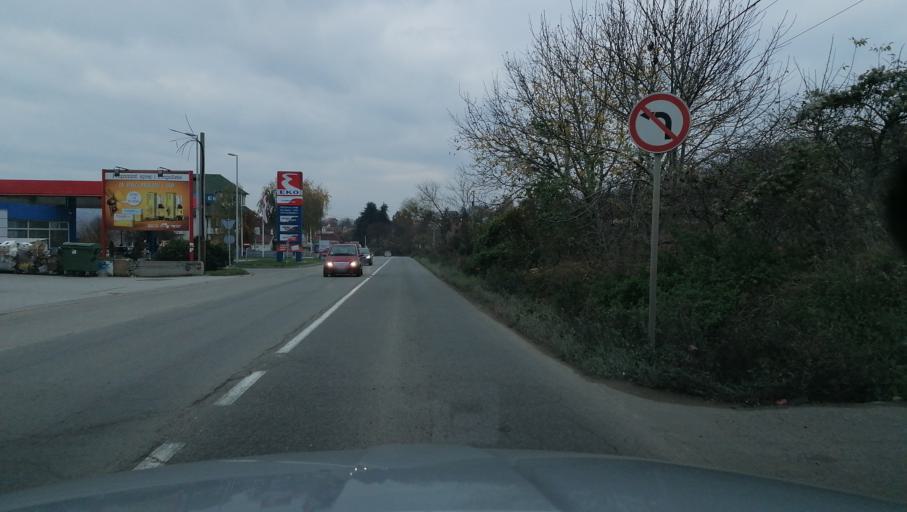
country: RS
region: Central Serbia
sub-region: Belgrade
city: Zvezdara
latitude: 44.7503
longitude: 20.5848
